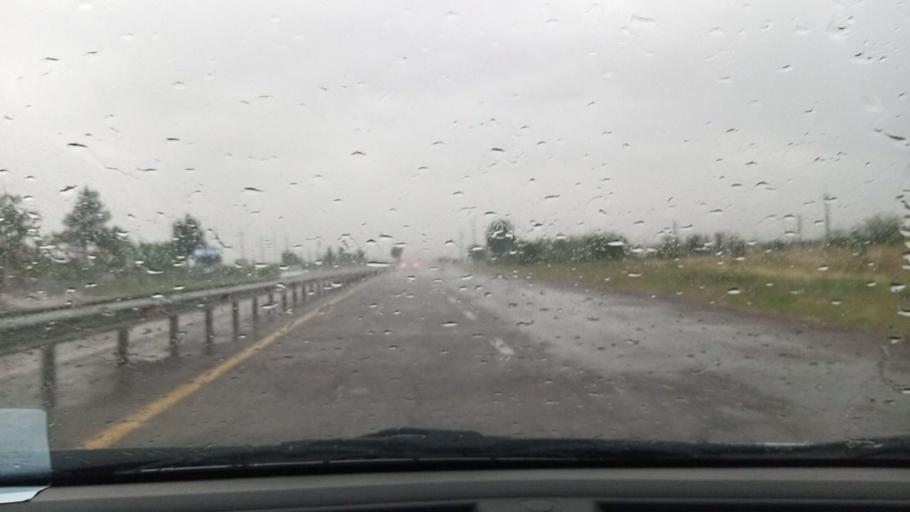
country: UZ
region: Toshkent
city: Ohangaron
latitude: 40.9326
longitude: 69.5918
